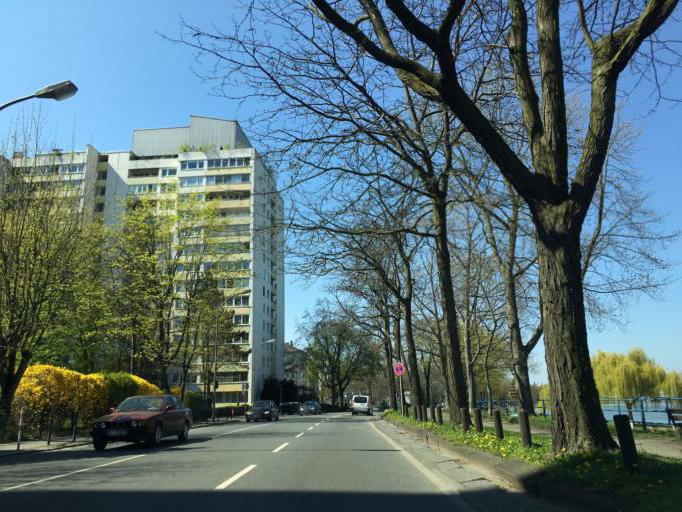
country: DE
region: Hesse
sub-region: Regierungsbezirk Darmstadt
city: Offenbach
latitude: 50.1071
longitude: 8.7712
